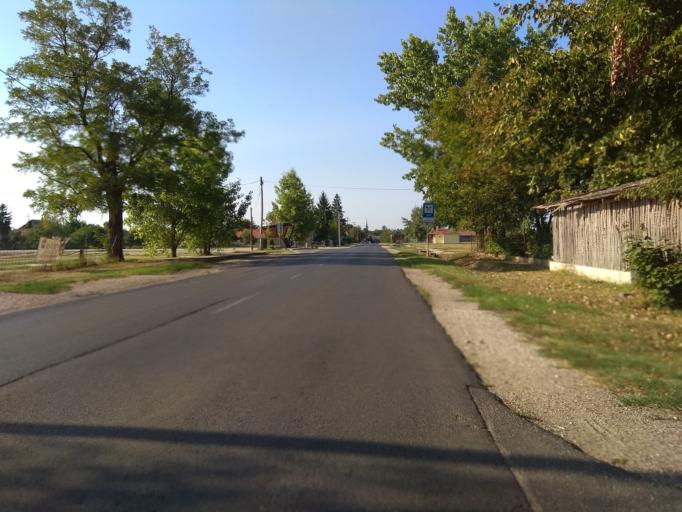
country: HU
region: Borsod-Abauj-Zemplen
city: Onod
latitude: 47.9957
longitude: 20.9209
